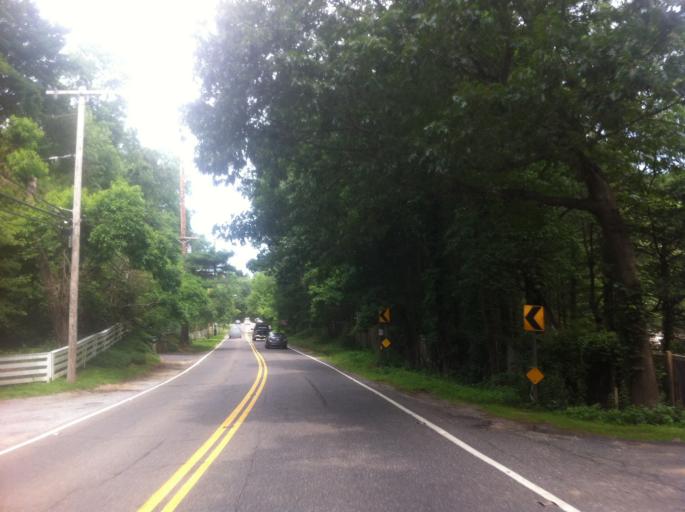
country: US
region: New York
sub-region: Nassau County
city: Syosset
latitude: 40.8460
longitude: -73.5030
